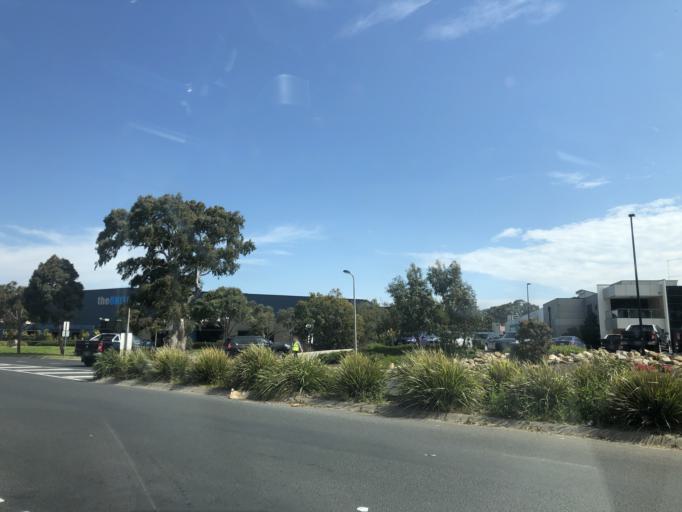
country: AU
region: Victoria
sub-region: Casey
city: Hampton Park
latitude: -38.0355
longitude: 145.2414
